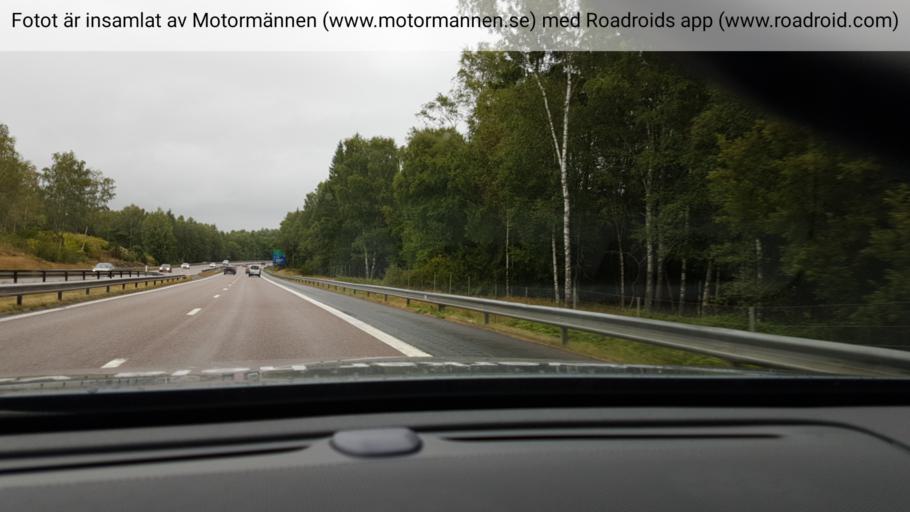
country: SE
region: Vaestra Goetaland
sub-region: Lerums Kommun
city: Lerum
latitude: 57.7444
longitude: 12.2202
